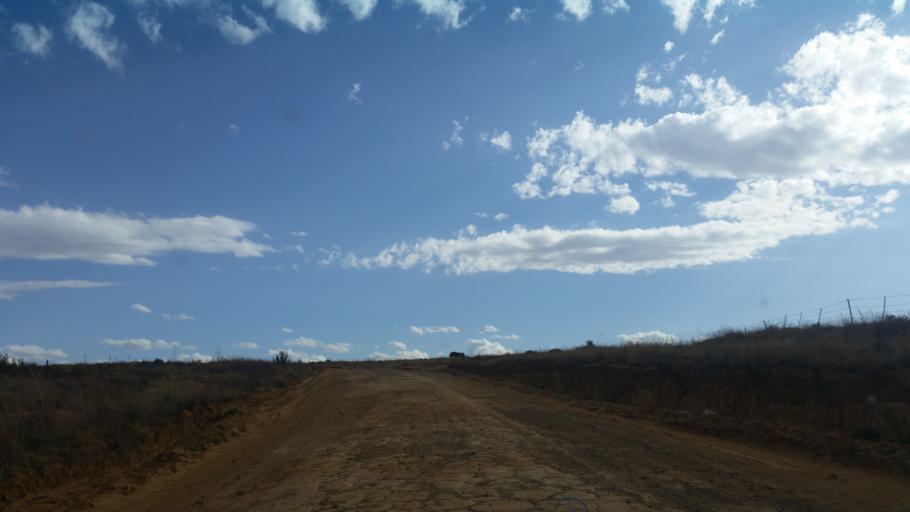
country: ZA
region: Orange Free State
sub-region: Thabo Mofutsanyana District Municipality
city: Phuthaditjhaba
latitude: -28.3513
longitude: 28.6049
